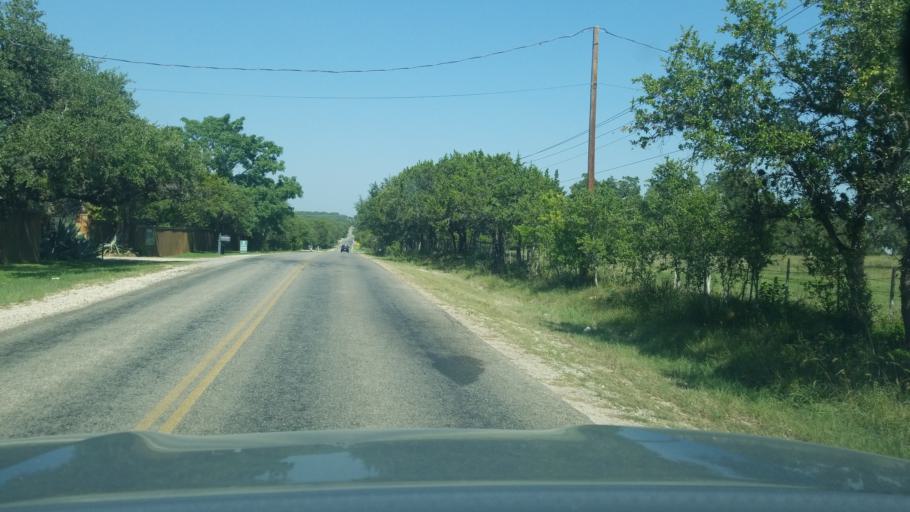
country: US
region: Texas
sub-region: Kendall County
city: Boerne
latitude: 29.7871
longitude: -98.6813
